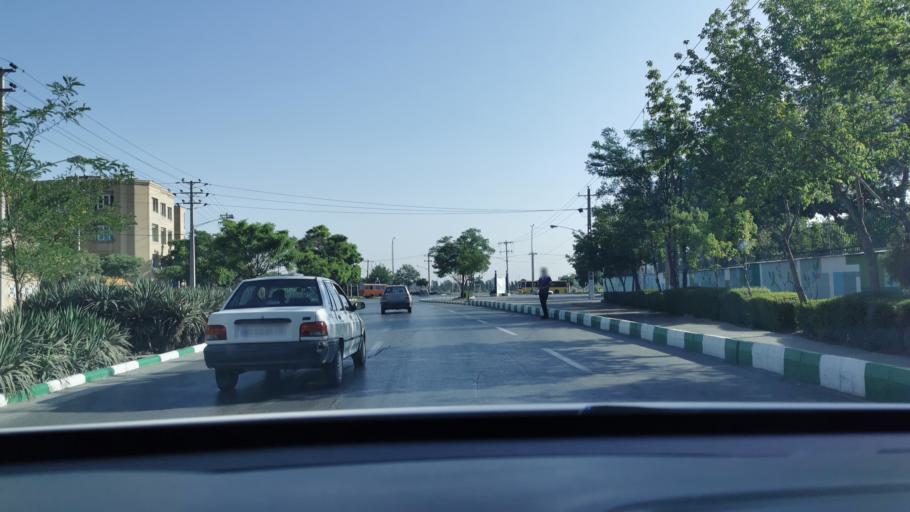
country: IR
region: Razavi Khorasan
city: Mashhad
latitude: 36.3399
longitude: 59.5075
